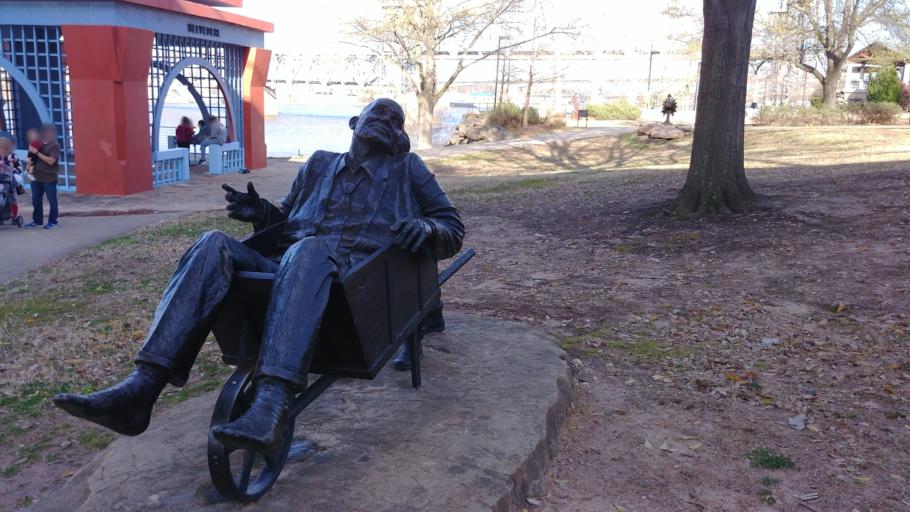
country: US
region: Arkansas
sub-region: Pulaski County
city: North Little Rock
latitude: 34.7494
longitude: -92.2692
